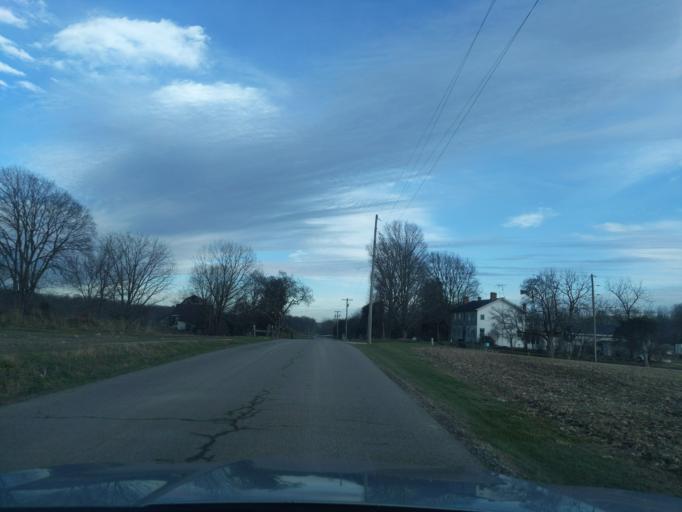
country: US
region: Indiana
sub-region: Decatur County
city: Westport
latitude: 39.2340
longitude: -85.5466
